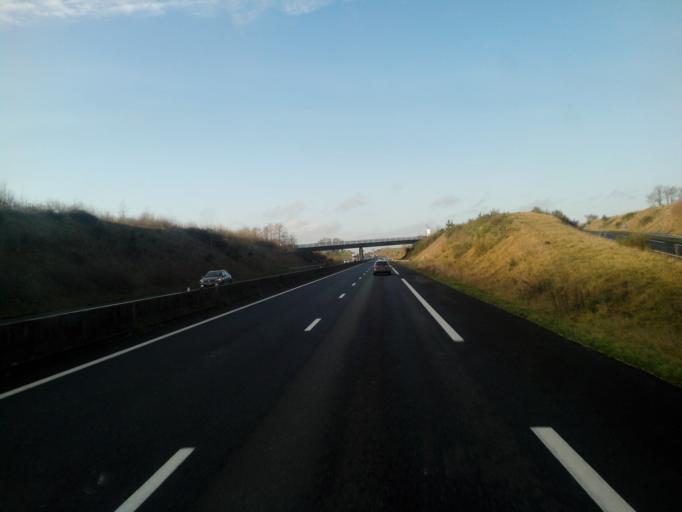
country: FR
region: Poitou-Charentes
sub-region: Departement des Deux-Sevres
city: Saint-Pierre-des-Echaubrognes
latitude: 46.9402
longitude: -0.7517
